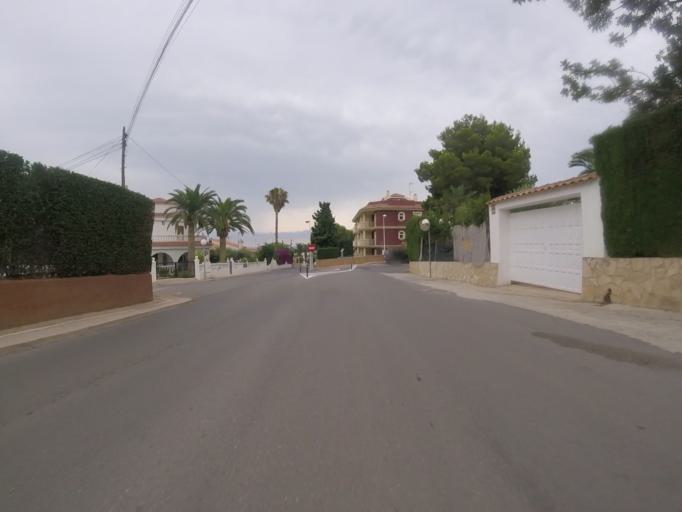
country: ES
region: Valencia
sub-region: Provincia de Castello
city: Alcoceber
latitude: 40.2587
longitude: 0.2893
